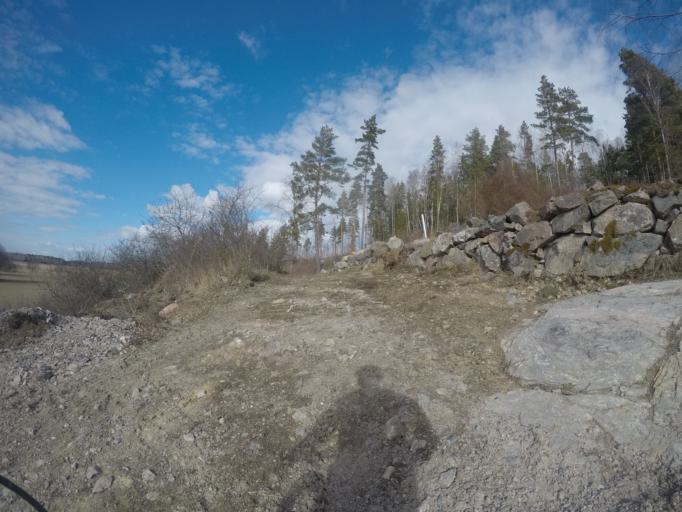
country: SE
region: Soedermanland
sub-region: Eskilstuna Kommun
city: Kvicksund
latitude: 59.4204
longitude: 16.2677
